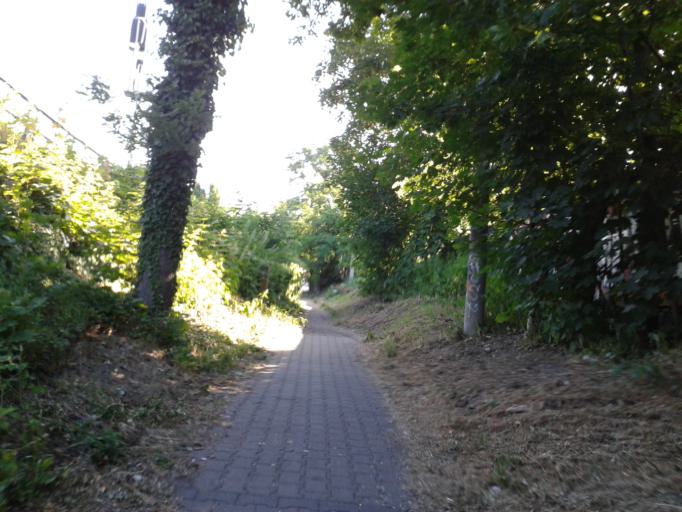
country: DE
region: Saxony
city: Albertstadt
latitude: 51.0765
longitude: 13.7530
